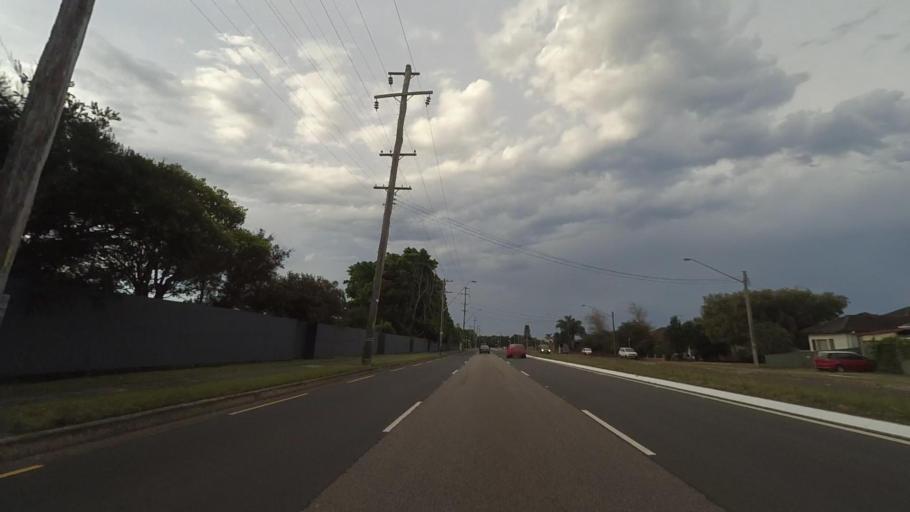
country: AU
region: New South Wales
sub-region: Shellharbour
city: Lake Illawarra
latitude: -34.5273
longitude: 150.8694
